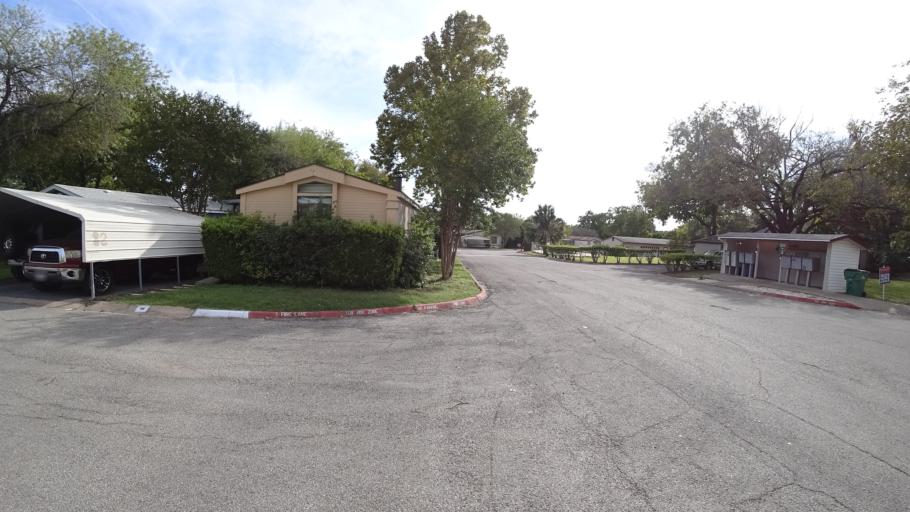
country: US
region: Texas
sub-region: Travis County
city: Onion Creek
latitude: 30.1995
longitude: -97.7568
